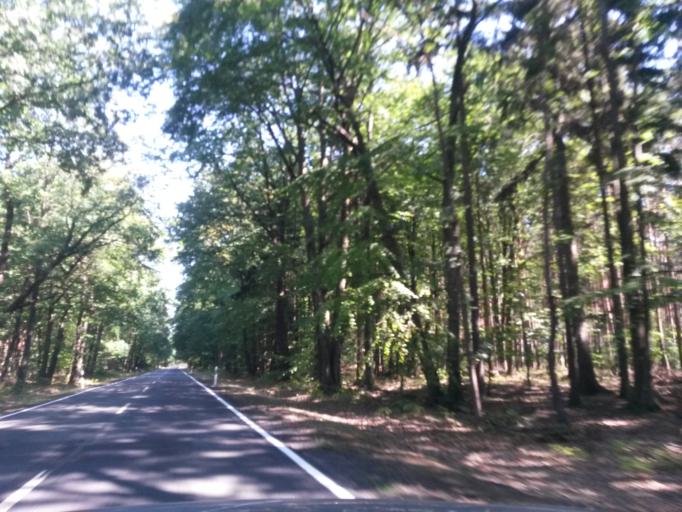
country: DE
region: Brandenburg
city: Wiesenburg
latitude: 52.0802
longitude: 12.4092
